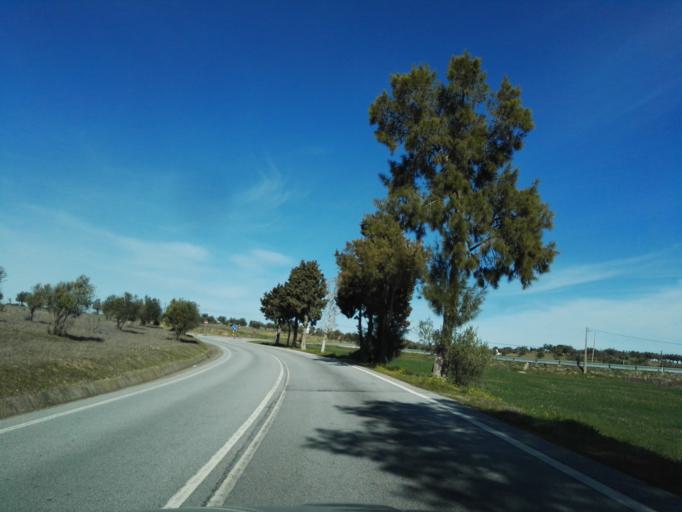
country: PT
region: Portalegre
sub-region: Arronches
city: Arronches
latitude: 39.1331
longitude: -7.2909
